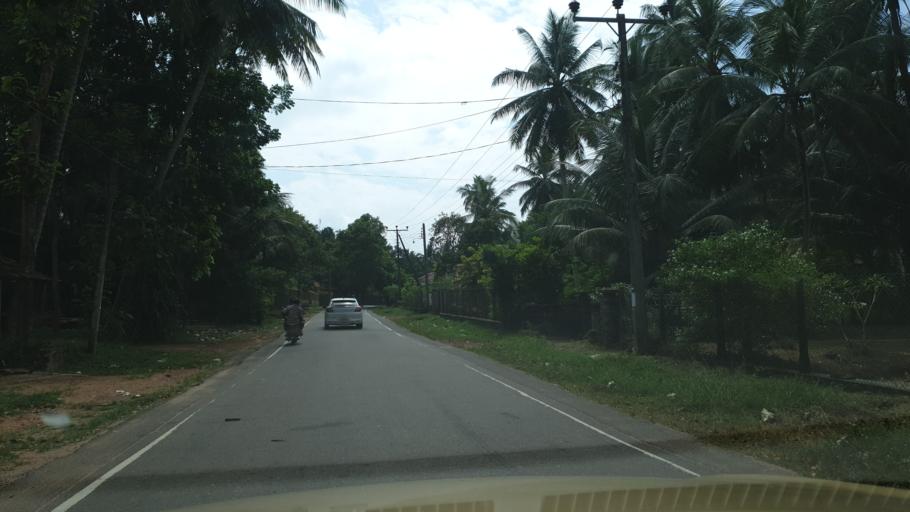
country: LK
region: North Western
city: Kuliyapitiya
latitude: 7.3457
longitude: 79.9862
